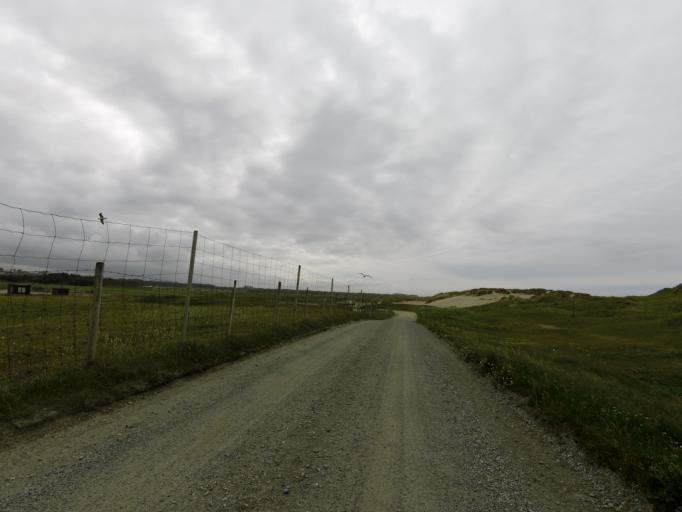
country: NO
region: Rogaland
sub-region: Klepp
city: Kleppe
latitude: 58.8003
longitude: 5.5515
